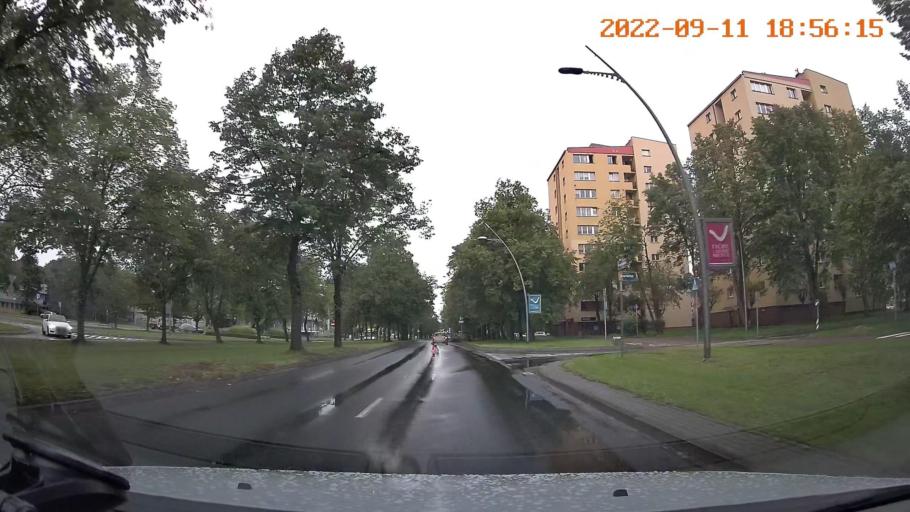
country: PL
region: Silesian Voivodeship
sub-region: Tychy
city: Cielmice
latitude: 50.1136
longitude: 18.9969
